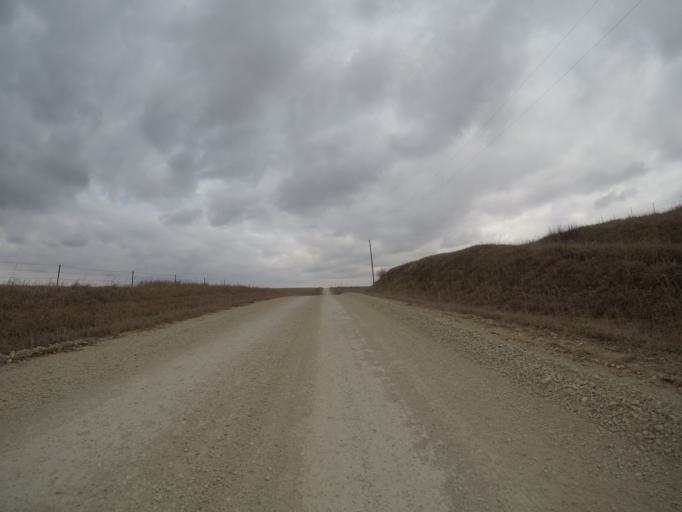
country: US
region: Kansas
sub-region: Morris County
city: Council Grove
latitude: 38.7532
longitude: -96.2794
